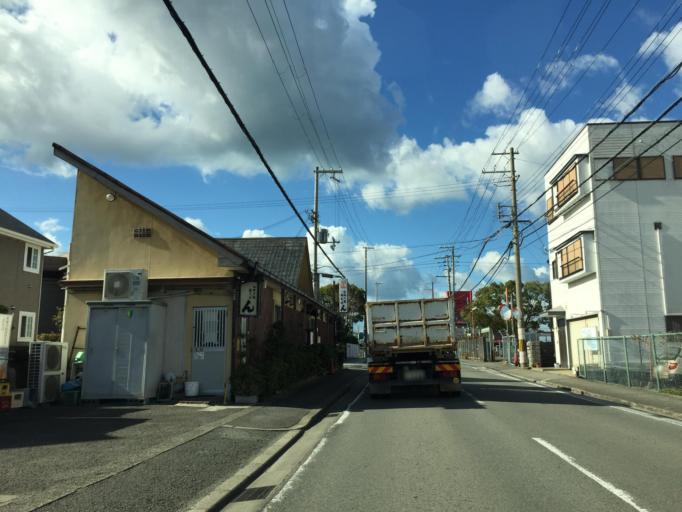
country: JP
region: Wakayama
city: Kainan
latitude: 34.1713
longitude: 135.1893
